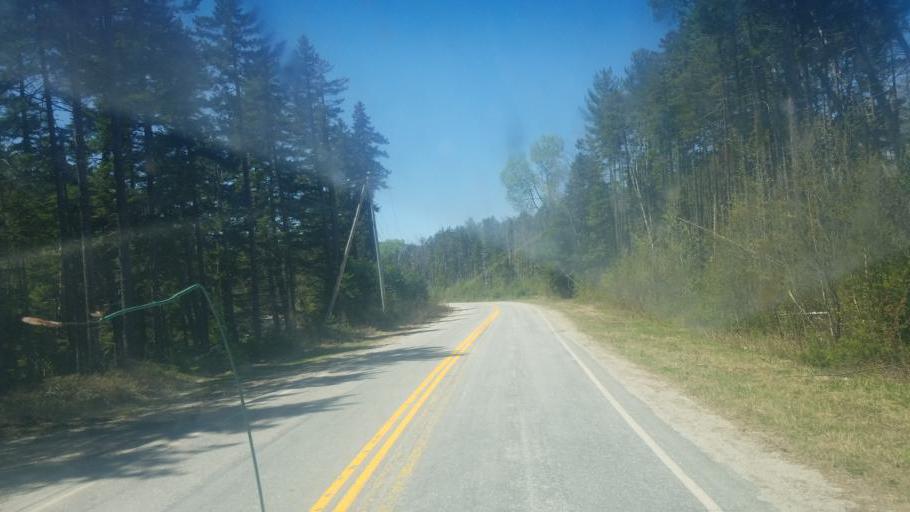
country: US
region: New Hampshire
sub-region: Coos County
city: Jefferson
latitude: 44.2649
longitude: -71.4213
